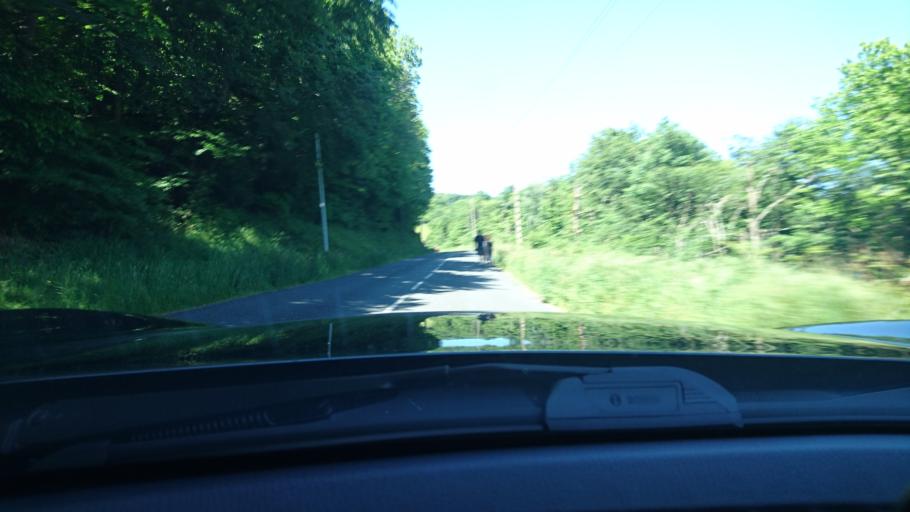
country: FR
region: Rhone-Alpes
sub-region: Departement du Rhone
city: Courzieu
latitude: 45.7126
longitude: 4.5890
